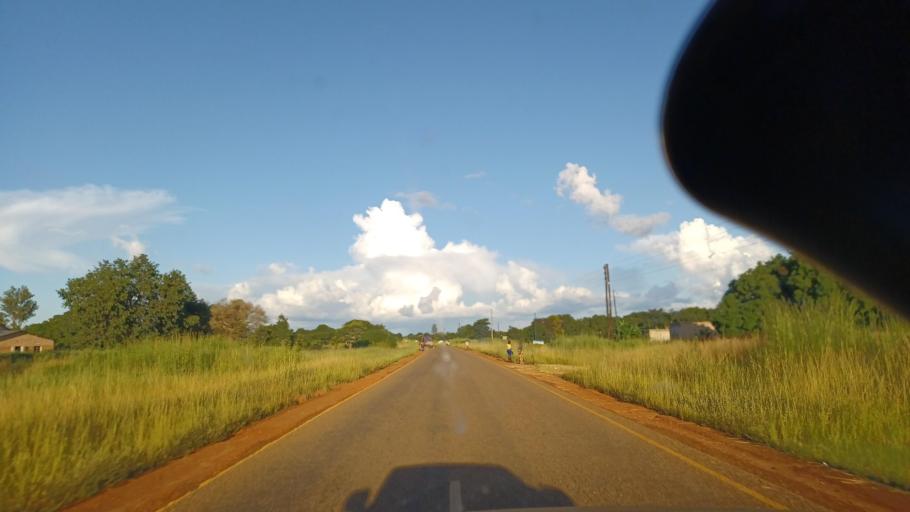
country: ZM
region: North-Western
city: Kalengwa
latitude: -13.1422
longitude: 25.0275
